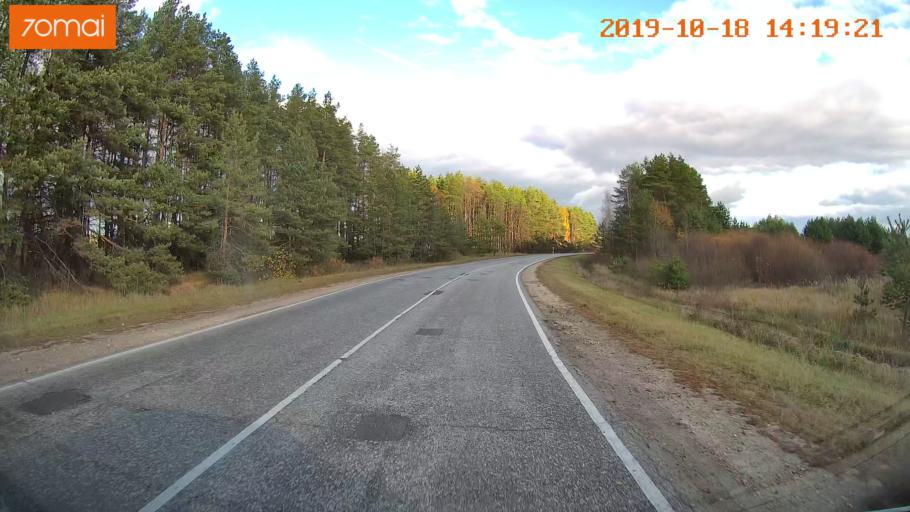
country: RU
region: Rjazan
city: Tuma
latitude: 55.1415
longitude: 40.4081
